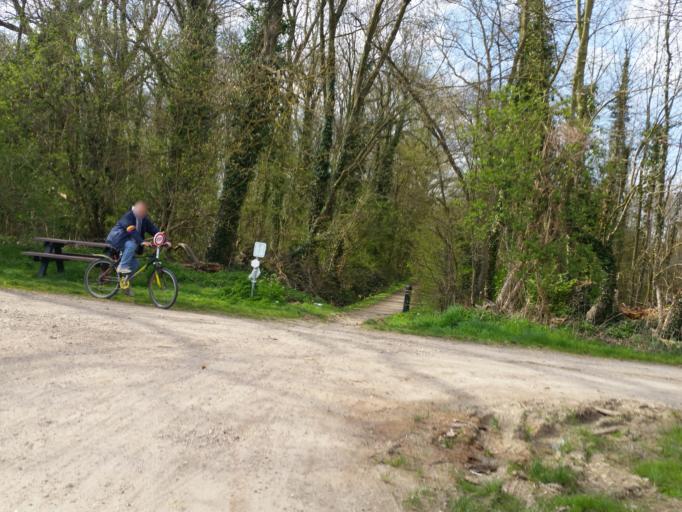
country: BE
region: Flanders
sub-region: Provincie Vlaams-Brabant
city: Kampenhout
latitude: 50.9262
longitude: 4.5529
